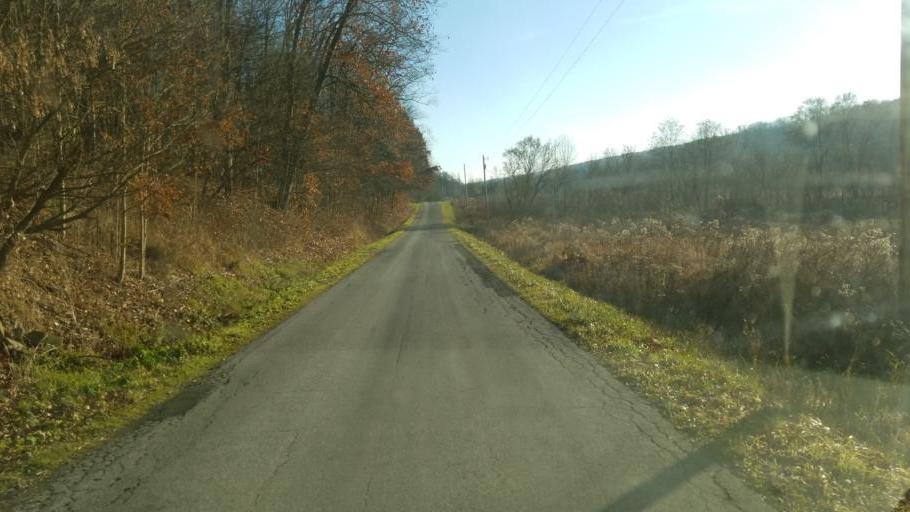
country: US
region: Ohio
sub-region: Wayne County
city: Wooster
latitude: 40.8997
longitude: -82.0079
